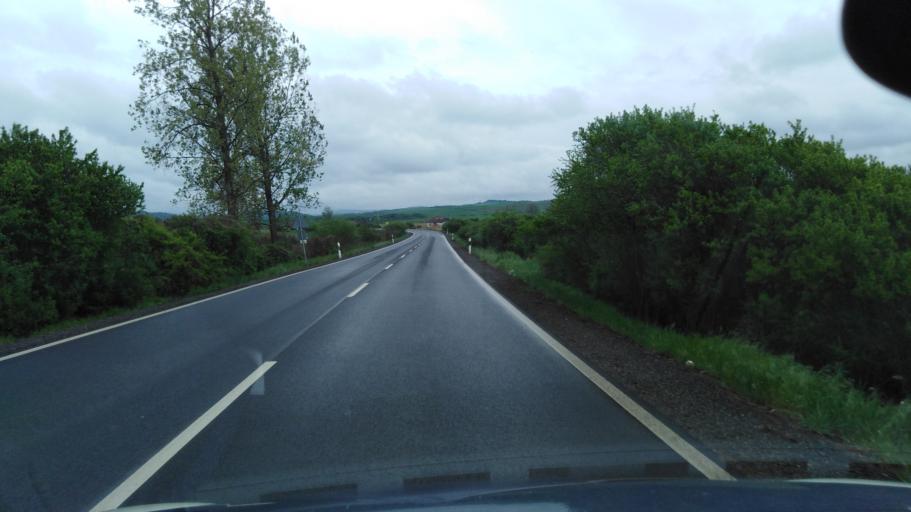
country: HU
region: Nograd
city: Karancskeszi
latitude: 48.1180
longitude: 19.6517
